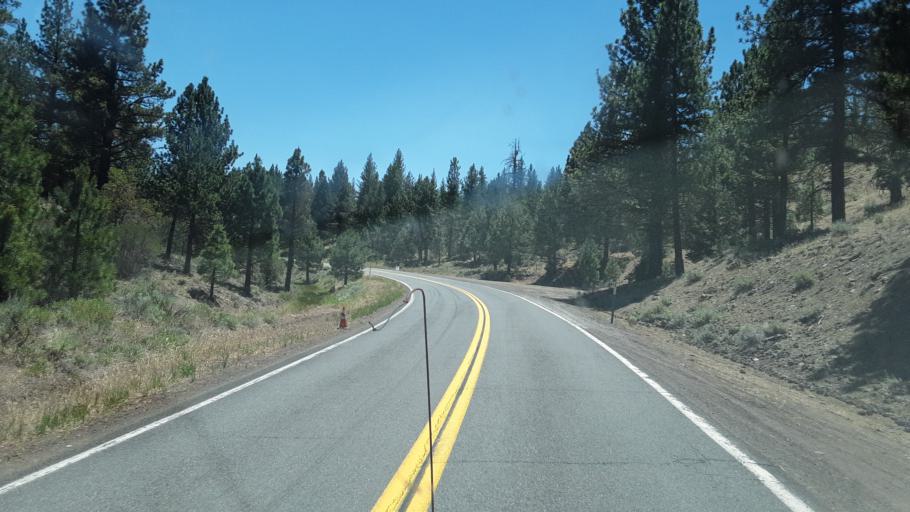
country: US
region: California
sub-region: Modoc County
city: Alturas
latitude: 41.0031
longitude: -120.8118
